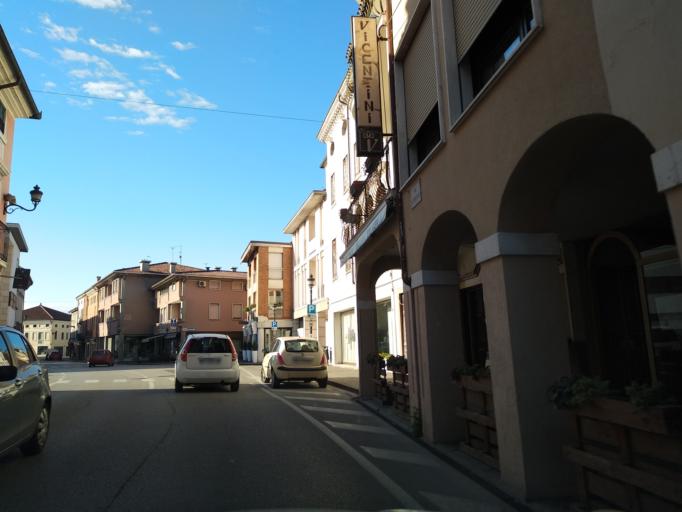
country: IT
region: Veneto
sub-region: Provincia di Vicenza
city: Camisano Vicentino
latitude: 45.5224
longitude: 11.7134
